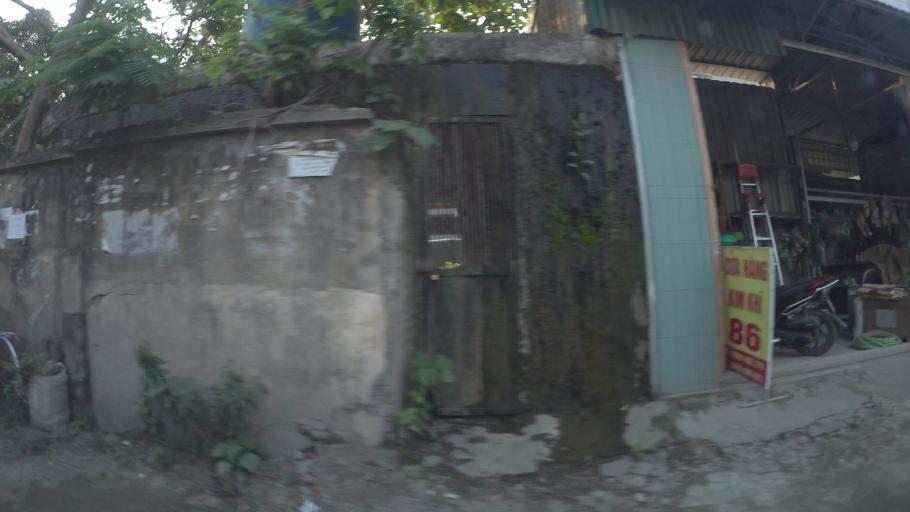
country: VN
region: Ha Noi
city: Van Dien
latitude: 20.9404
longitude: 105.8407
